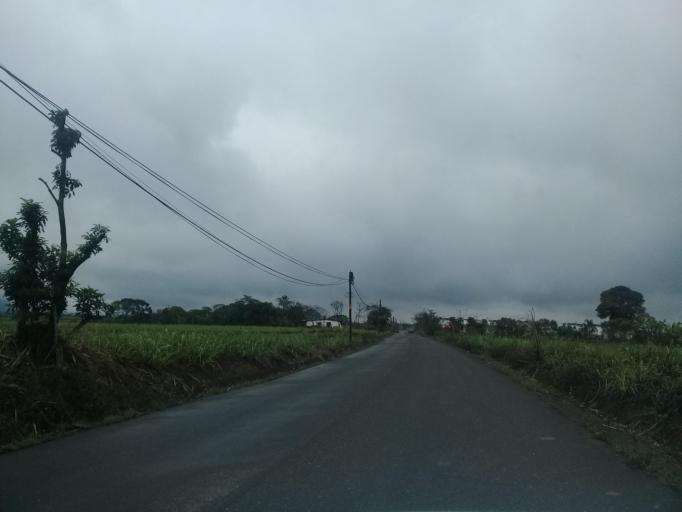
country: MX
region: Veracruz
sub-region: Amatlan de los Reyes
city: Trapiche Viejo
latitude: 18.8318
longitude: -96.9559
